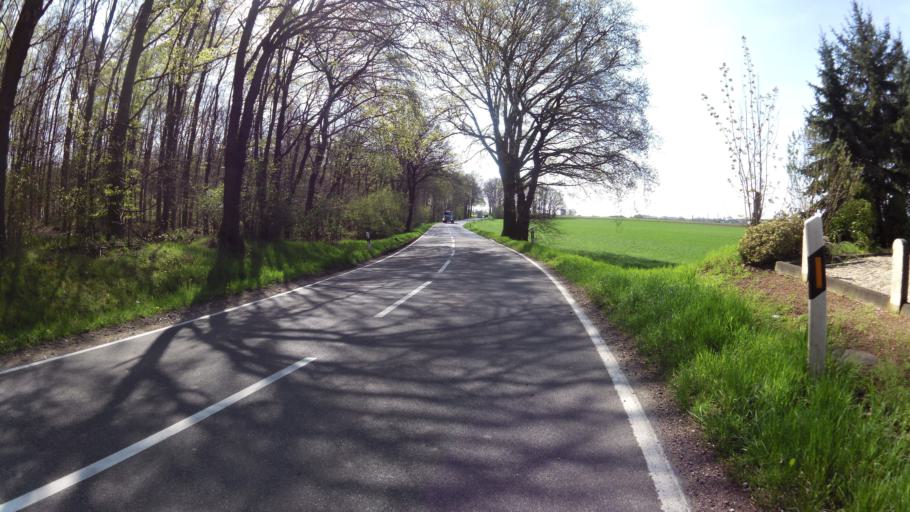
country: DE
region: North Rhine-Westphalia
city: Geilenkirchen
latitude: 50.9909
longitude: 6.0702
